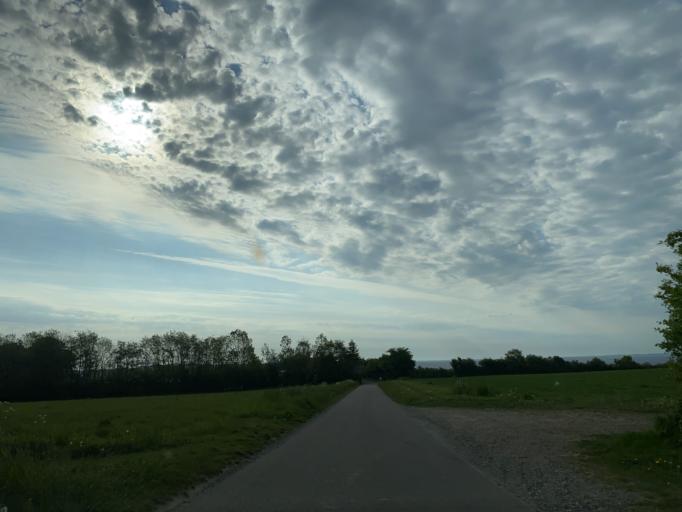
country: DK
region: South Denmark
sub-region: Sonderborg Kommune
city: Dybbol
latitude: 54.9028
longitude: 9.7600
